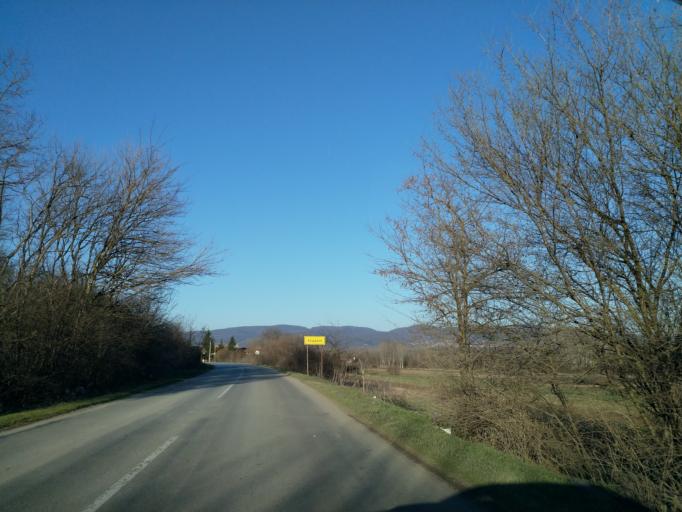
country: RS
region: Central Serbia
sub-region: Pomoravski Okrug
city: Paracin
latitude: 43.8811
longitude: 21.4753
